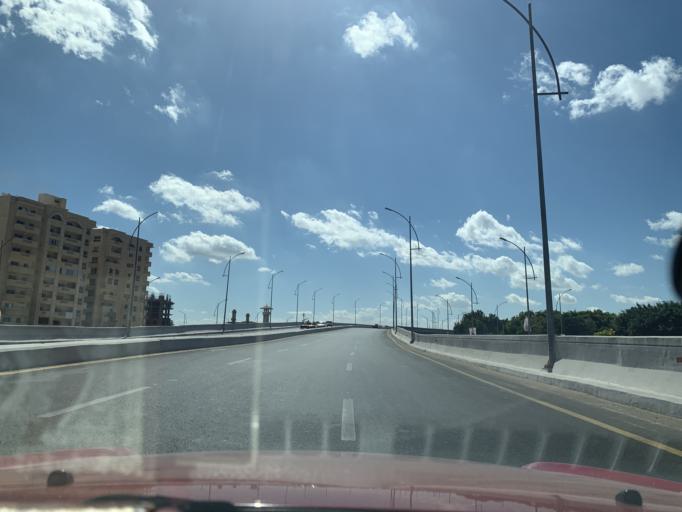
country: EG
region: Alexandria
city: Alexandria
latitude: 31.2023
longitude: 29.9536
